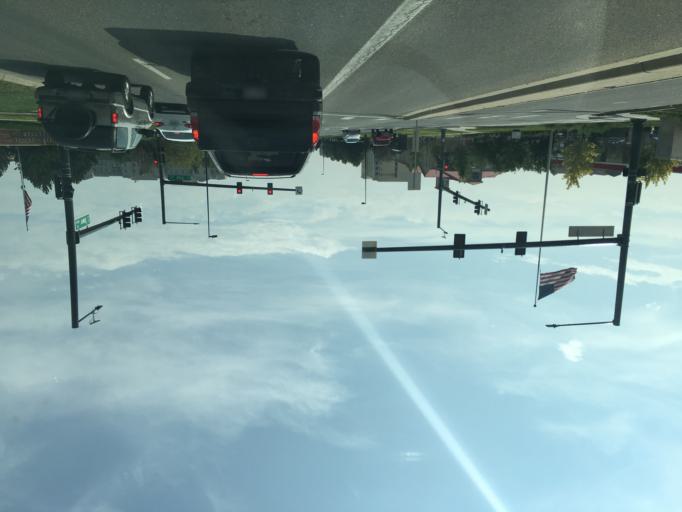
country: US
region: Colorado
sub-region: Adams County
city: Aurora
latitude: 39.8260
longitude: -104.7720
